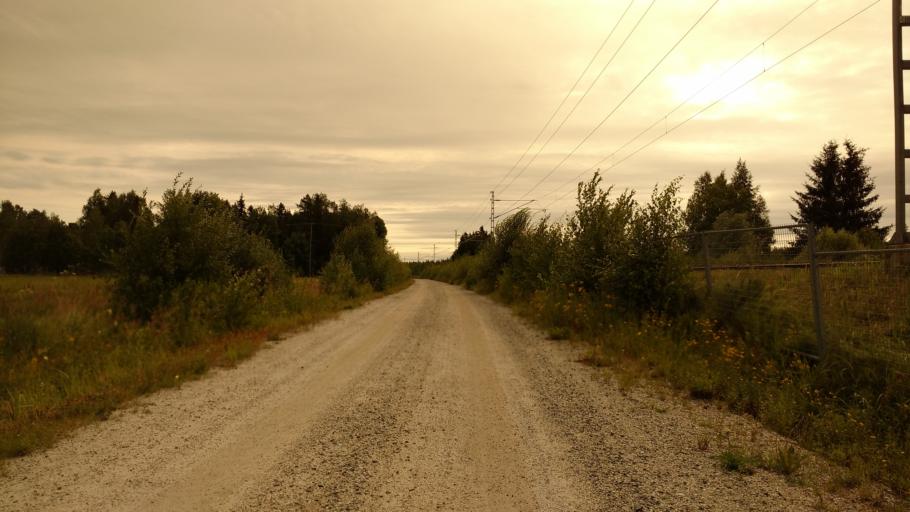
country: FI
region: Varsinais-Suomi
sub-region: Turku
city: Kaarina
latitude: 60.4438
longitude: 22.4245
